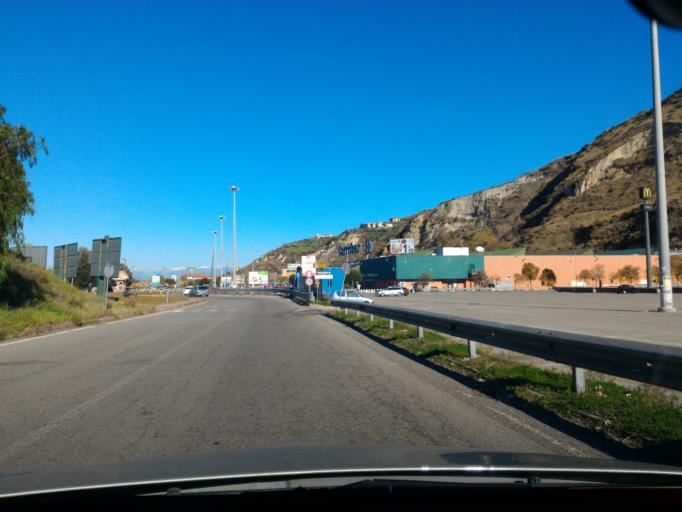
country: IT
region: Calabria
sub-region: Provincia di Cosenza
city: Cosenza
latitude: 39.3104
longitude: 16.2630
